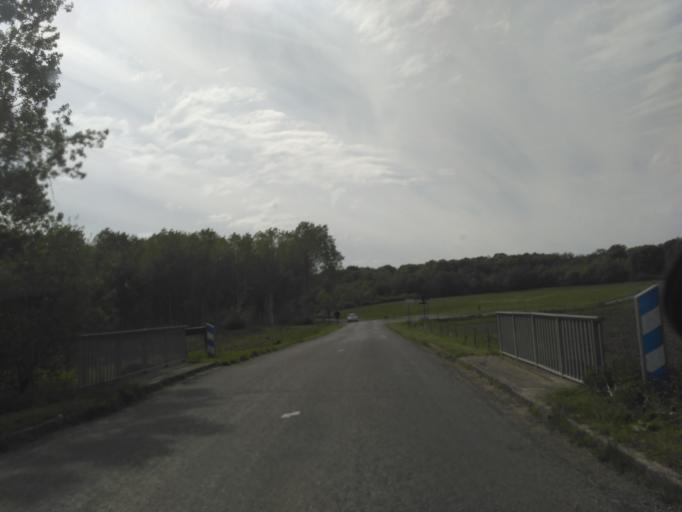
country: FR
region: Ile-de-France
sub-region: Departement de Seine-et-Marne
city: Chaumes-en-Brie
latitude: 48.6663
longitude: 2.8221
